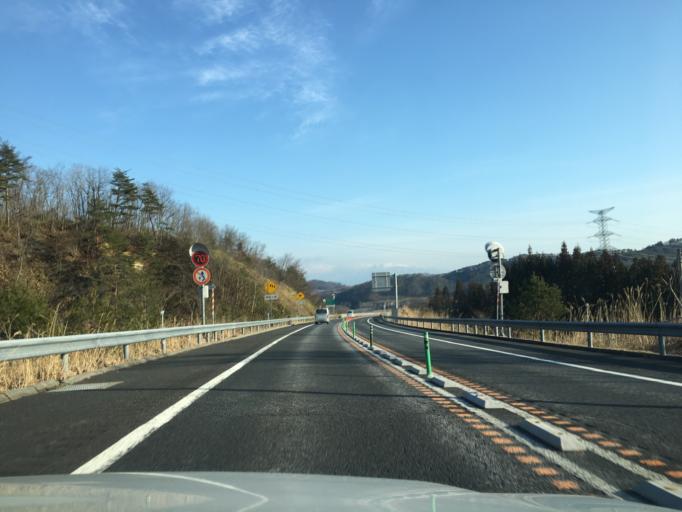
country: JP
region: Yamagata
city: Sagae
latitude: 38.4179
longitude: 140.1871
